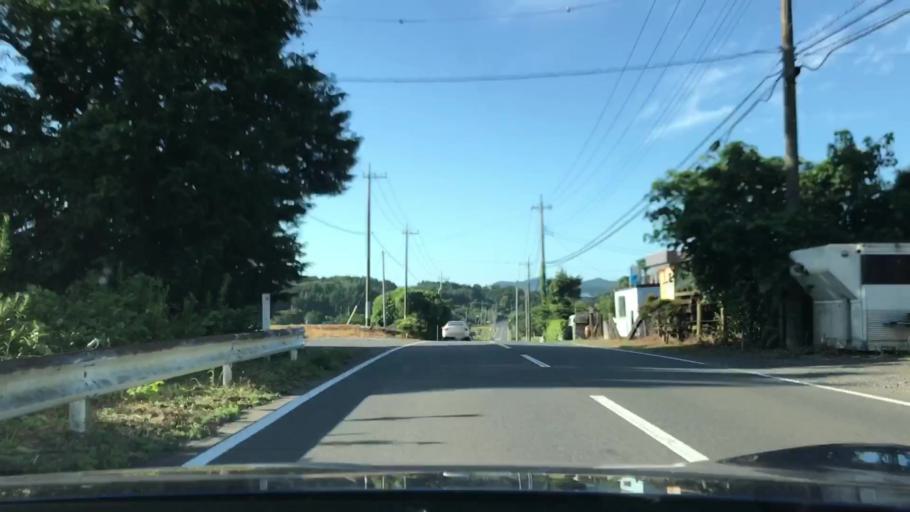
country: JP
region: Ibaraki
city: Makabe
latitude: 36.2406
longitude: 140.1650
